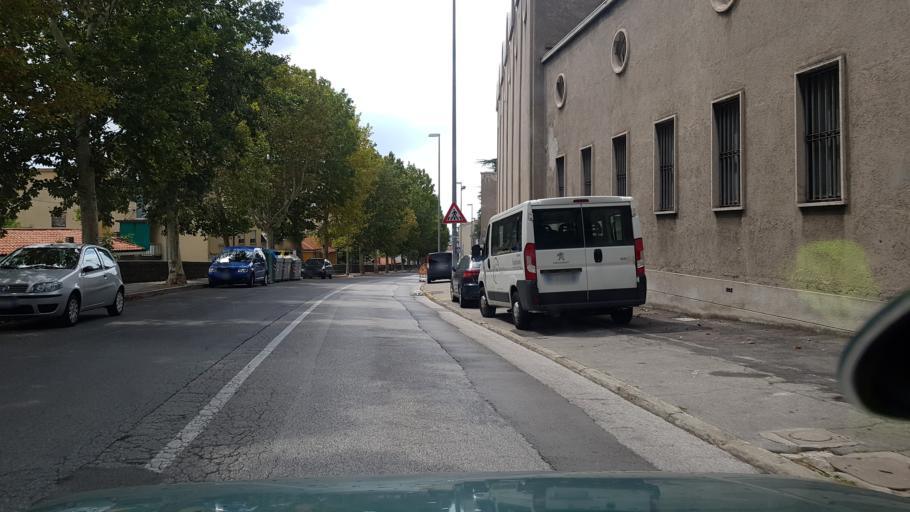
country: IT
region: Friuli Venezia Giulia
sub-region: Provincia di Trieste
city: Trieste
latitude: 45.6419
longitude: 13.8052
